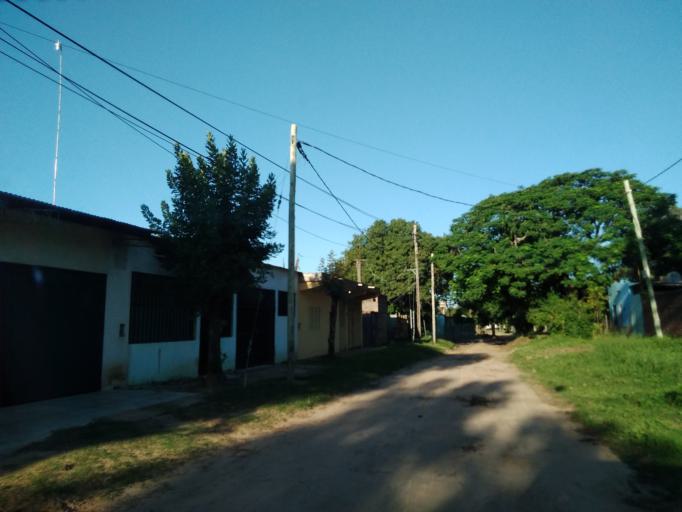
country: AR
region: Corrientes
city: Corrientes
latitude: -27.5029
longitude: -58.8052
